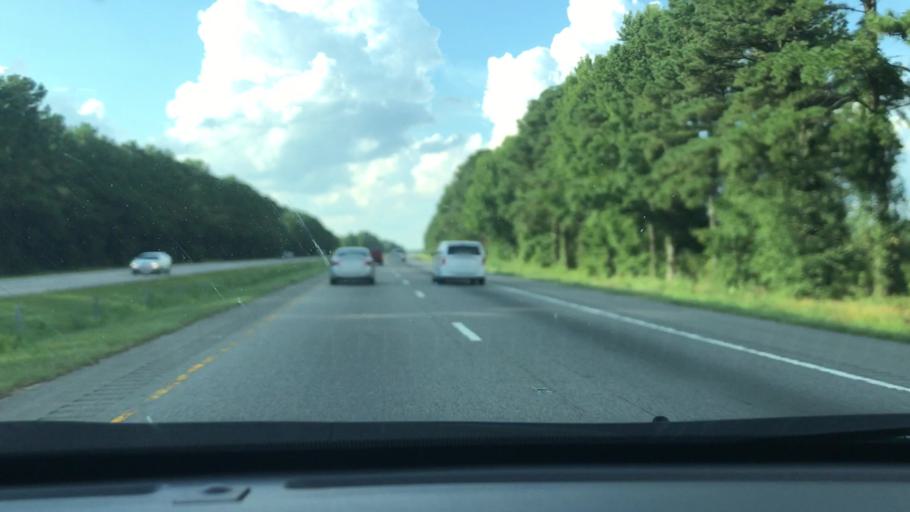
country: US
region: North Carolina
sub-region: Robeson County
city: Saint Pauls
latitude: 34.7589
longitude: -78.9969
